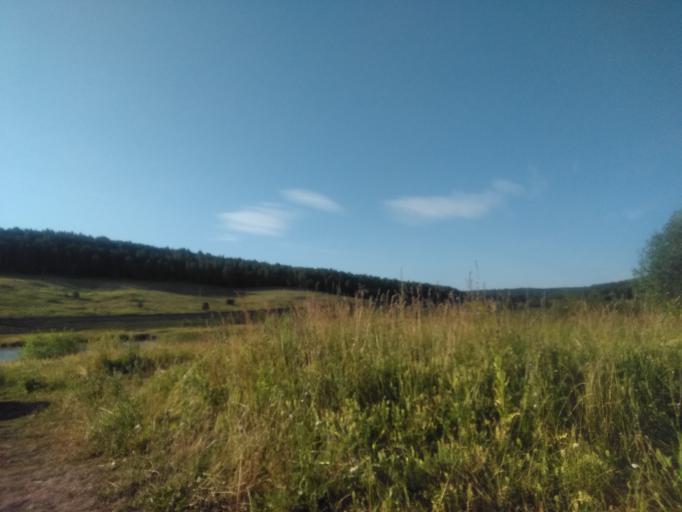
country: RU
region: Tatarstan
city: Russkiy Aktash
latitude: 54.8807
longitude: 52.0747
